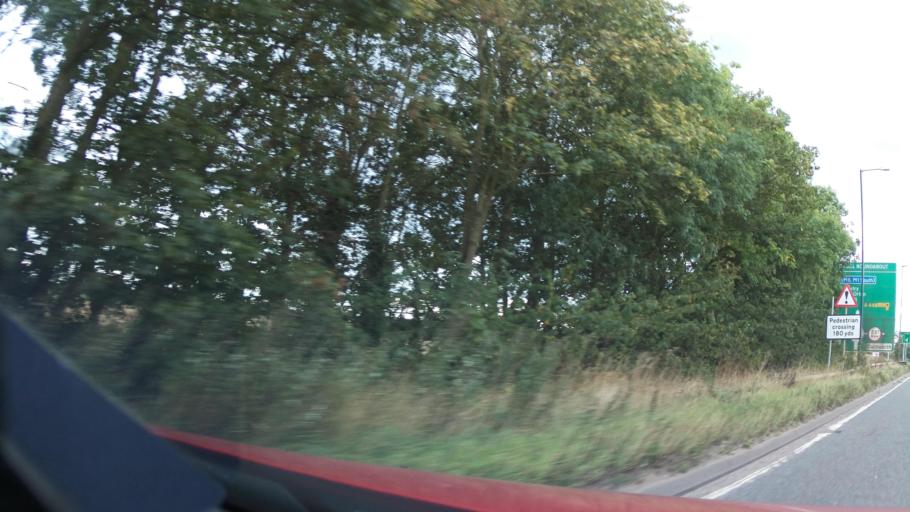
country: GB
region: England
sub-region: Warwickshire
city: Curdworth
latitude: 52.5319
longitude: -1.7234
